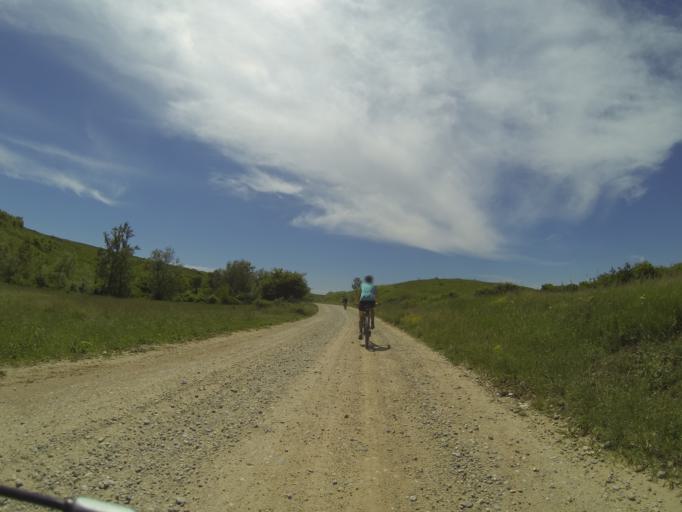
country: RO
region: Dolj
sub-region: Comuna Teslui
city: Teslui
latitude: 44.2005
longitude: 24.1335
